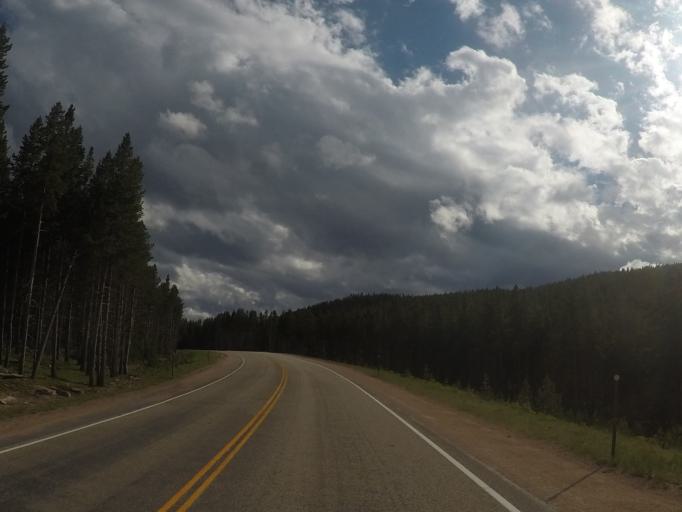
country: US
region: Wyoming
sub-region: Sheridan County
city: Sheridan
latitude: 44.7901
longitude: -107.4326
